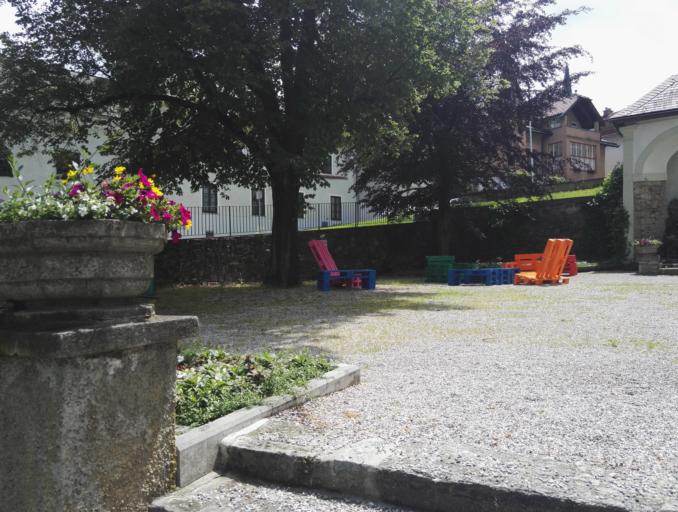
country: AT
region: Styria
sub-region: Politischer Bezirk Bruck-Muerzzuschlag
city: Muerzzuschlag
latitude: 47.6053
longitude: 15.6717
